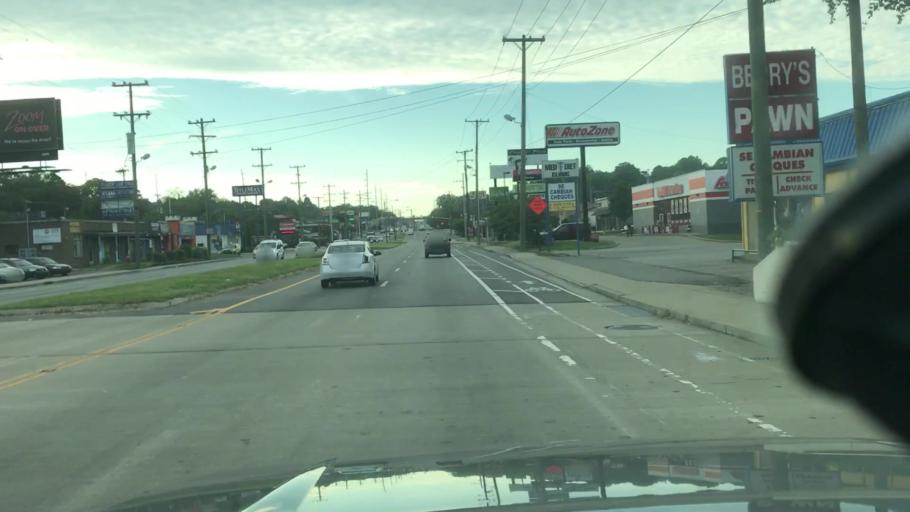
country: US
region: Tennessee
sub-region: Davidson County
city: Nashville
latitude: 36.1288
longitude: -86.7140
